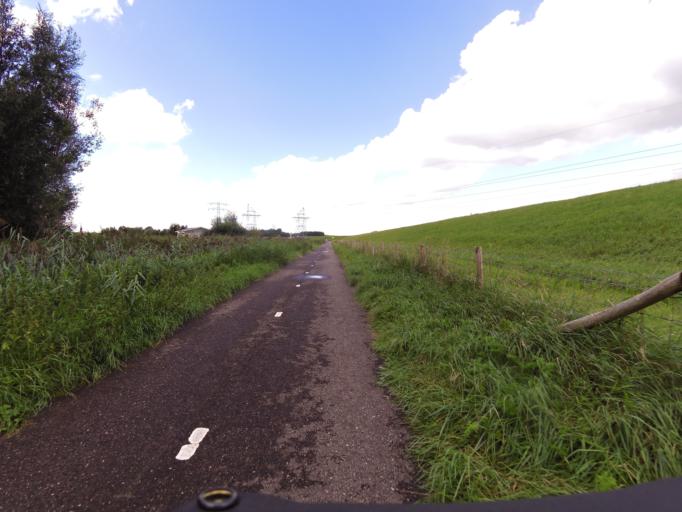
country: NL
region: North Brabant
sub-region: Gemeente Steenbergen
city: Dinteloord
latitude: 51.6987
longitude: 4.3354
